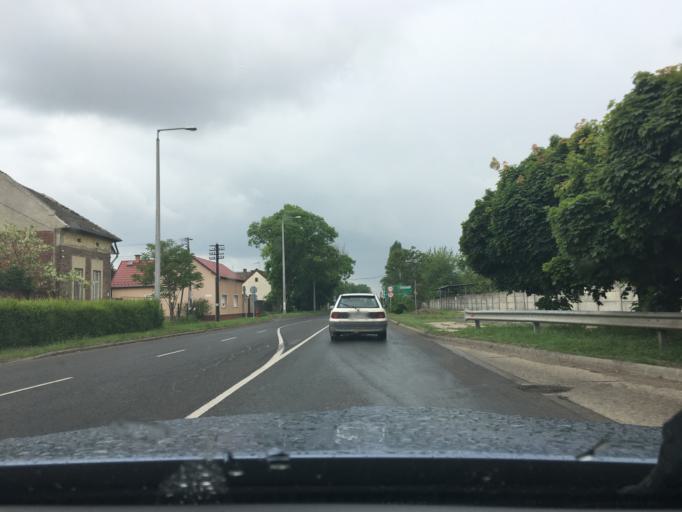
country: HU
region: Hajdu-Bihar
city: Debrecen
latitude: 47.5184
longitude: 21.6581
